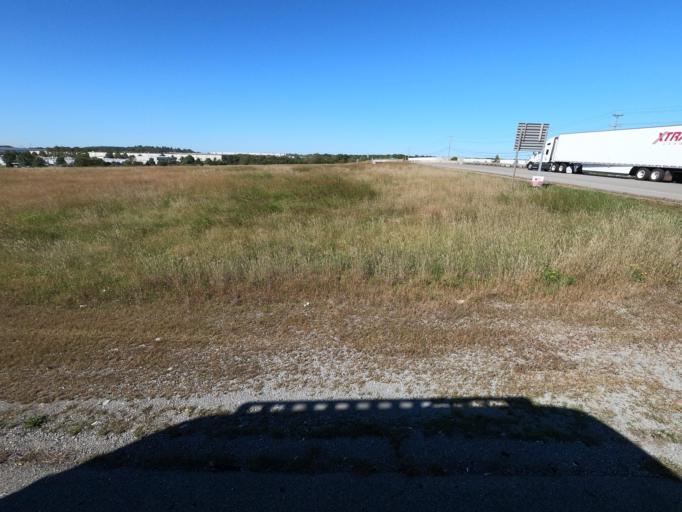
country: US
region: Tennessee
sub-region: Wilson County
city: Rural Hill
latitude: 36.0686
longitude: -86.4290
